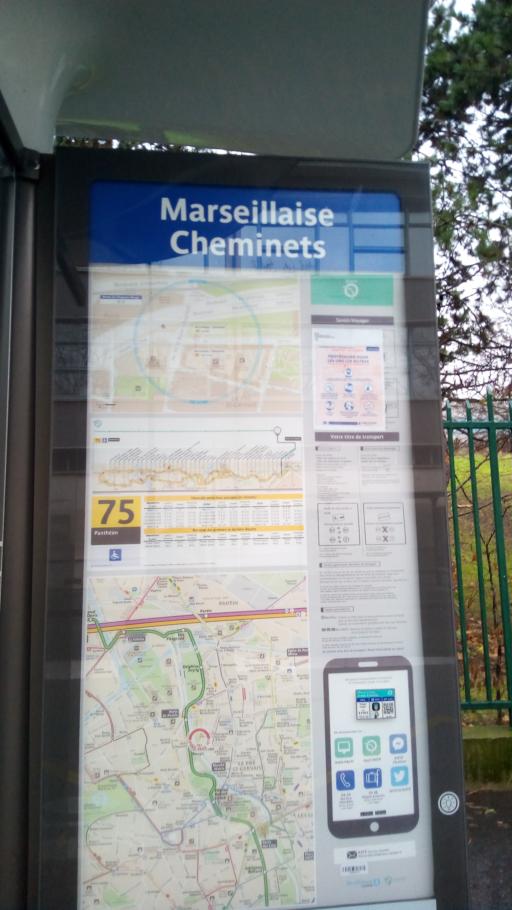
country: FR
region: Ile-de-France
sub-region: Departement de Seine-Saint-Denis
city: Le Pre-Saint-Gervais
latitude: 48.8863
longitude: 2.3981
